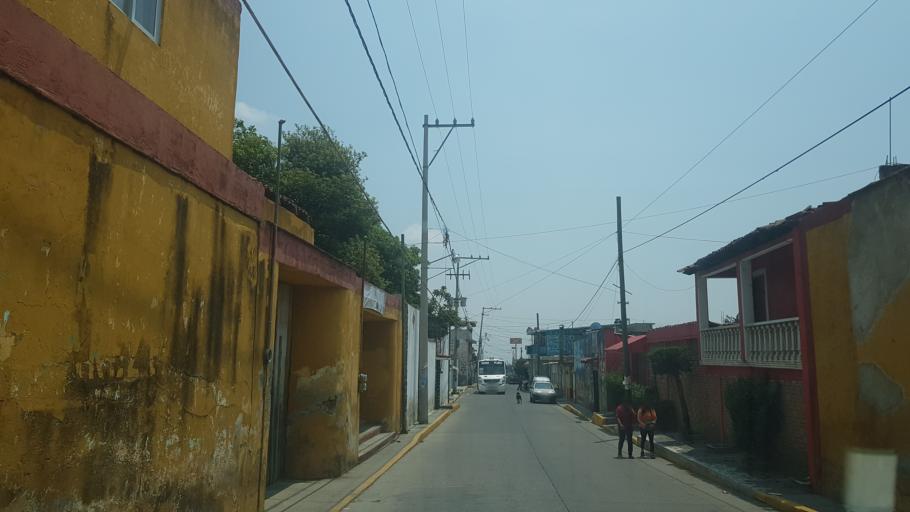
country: MX
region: Puebla
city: San Andres Calpan
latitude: 19.1051
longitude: -98.4632
